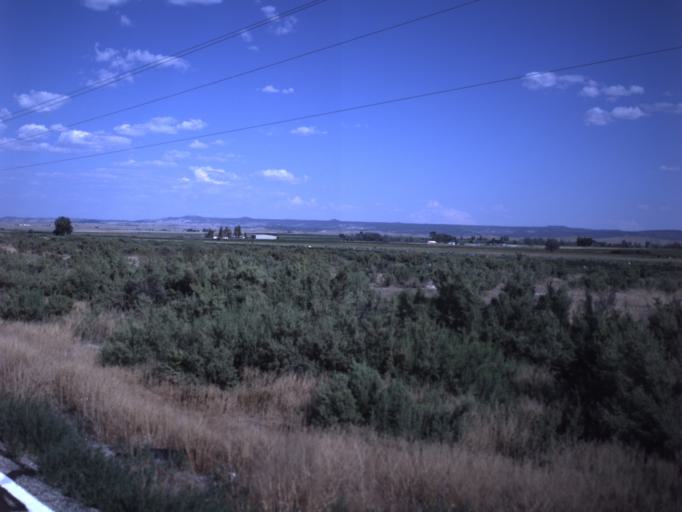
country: US
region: Utah
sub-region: Emery County
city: Huntington
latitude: 39.3462
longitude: -110.8832
